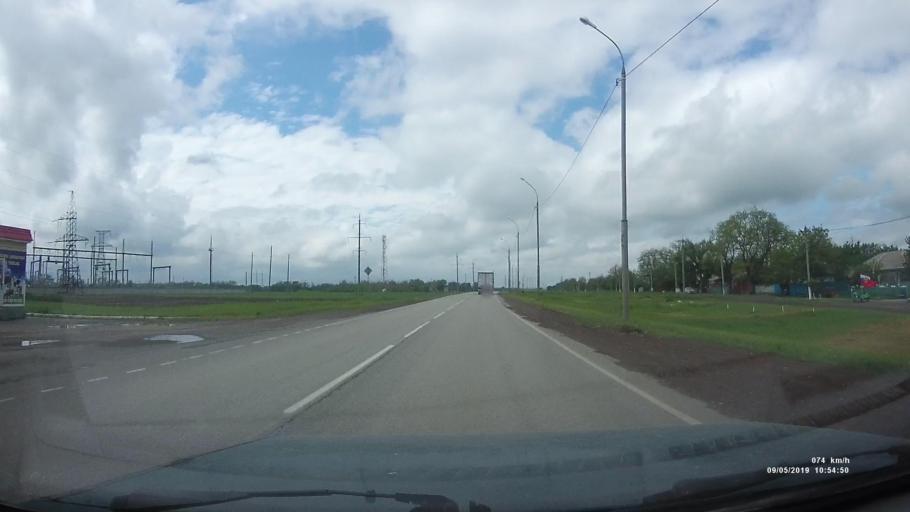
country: RU
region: Rostov
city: Peshkovo
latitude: 46.8748
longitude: 39.3255
